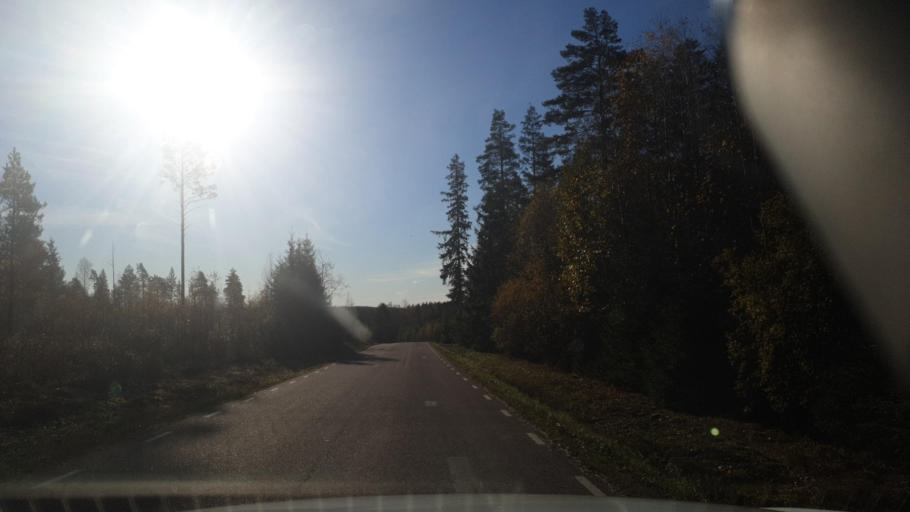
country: SE
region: Vaermland
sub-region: Karlstads Kommun
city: Edsvalla
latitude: 59.4737
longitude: 13.0804
